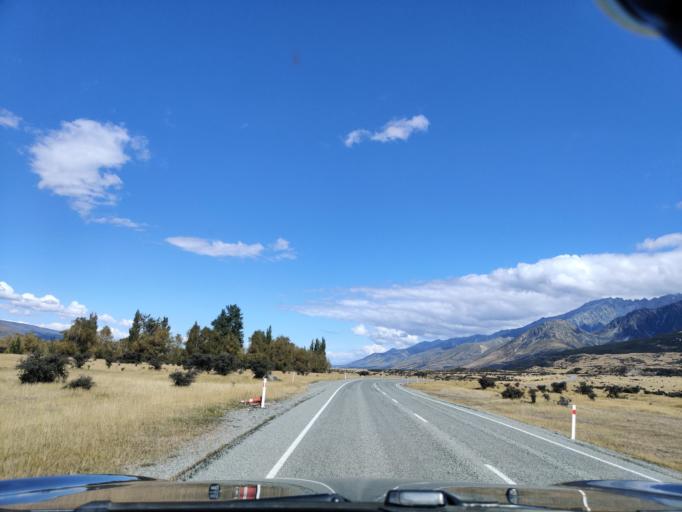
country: NZ
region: Canterbury
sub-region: Timaru District
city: Pleasant Point
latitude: -43.7887
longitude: 170.1196
